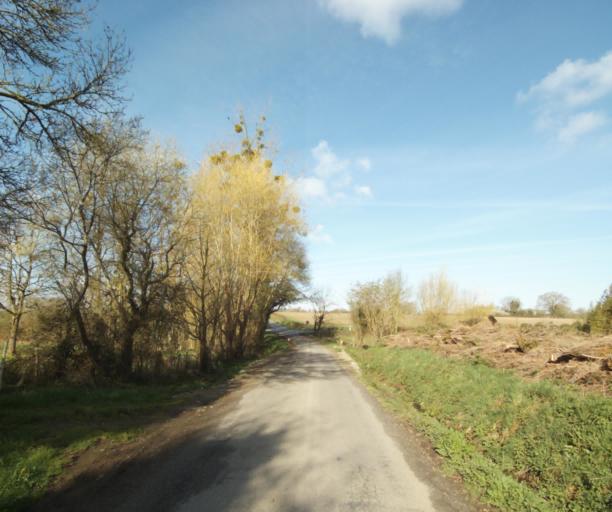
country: FR
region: Pays de la Loire
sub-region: Departement de la Loire-Atlantique
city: Bouvron
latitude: 47.4096
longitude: -1.8461
